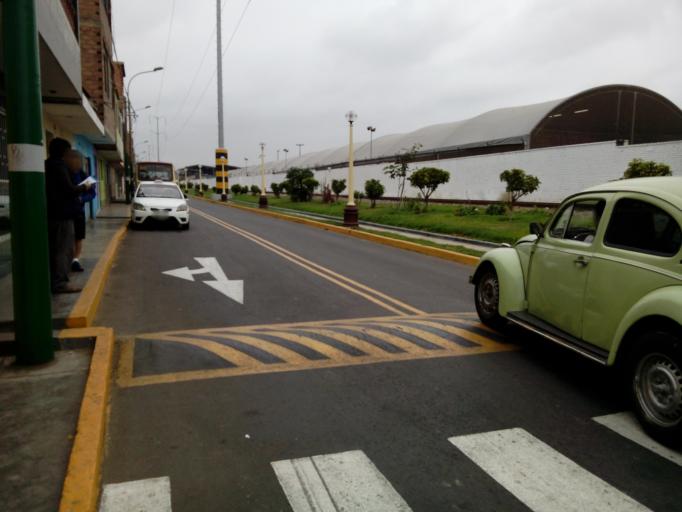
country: PE
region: Callao
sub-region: Callao
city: Callao
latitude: -12.0439
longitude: -77.0941
